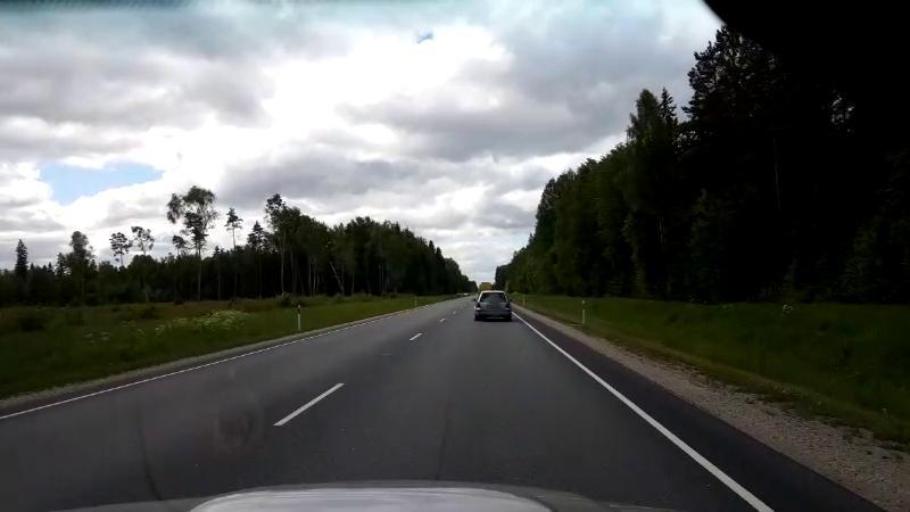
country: EE
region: Raplamaa
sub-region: Maerjamaa vald
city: Marjamaa
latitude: 58.7898
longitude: 24.4130
